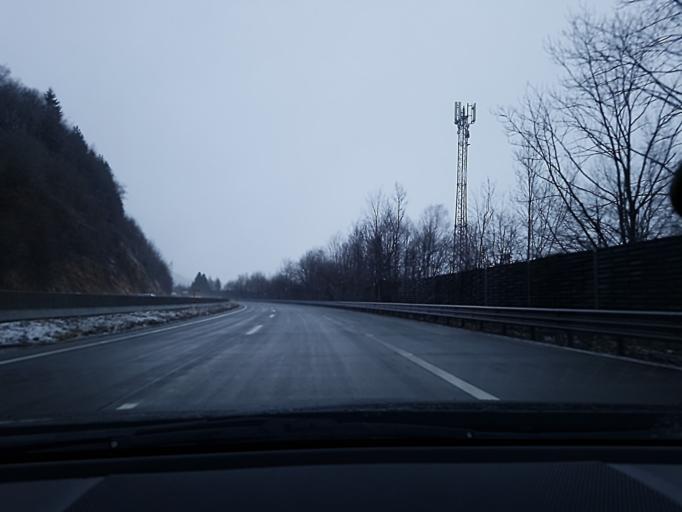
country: AT
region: Salzburg
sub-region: Politischer Bezirk Hallein
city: Kuchl
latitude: 47.6207
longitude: 13.1387
